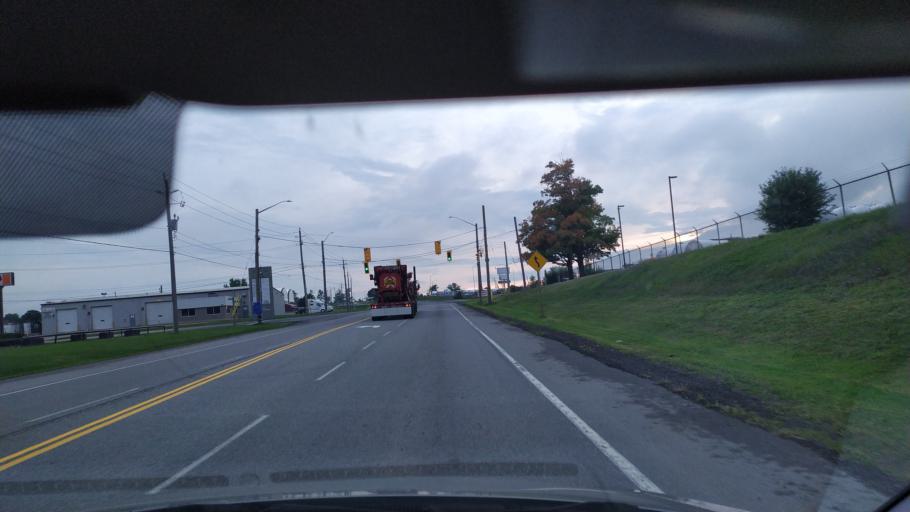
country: CA
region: Ontario
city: Kitchener
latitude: 43.3338
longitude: -80.4341
